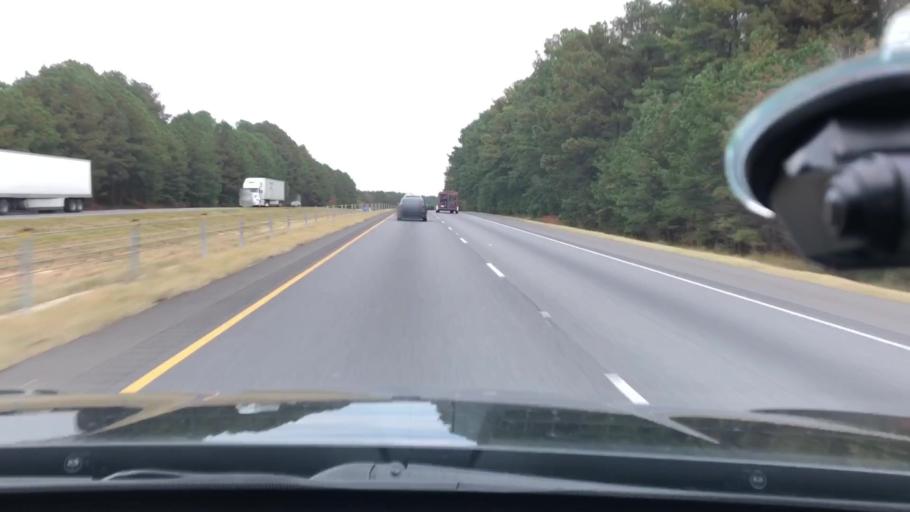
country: US
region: Arkansas
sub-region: Clark County
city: Arkadelphia
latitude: 34.2011
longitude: -93.0495
